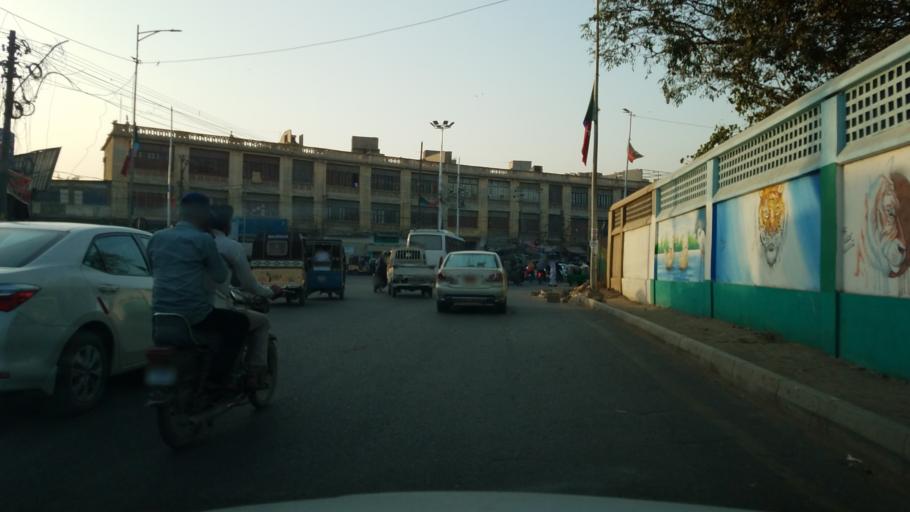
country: PK
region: Sindh
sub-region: Karachi District
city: Karachi
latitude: 24.8753
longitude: 67.0212
